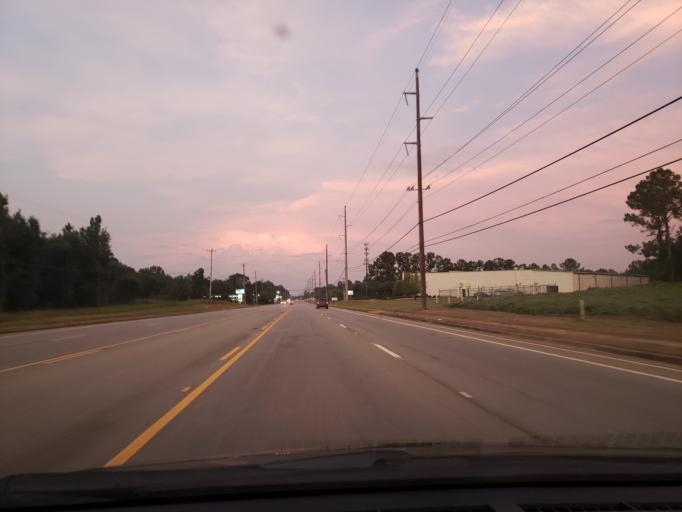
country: US
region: Georgia
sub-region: Dougherty County
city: Albany
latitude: 31.5856
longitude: -84.2401
